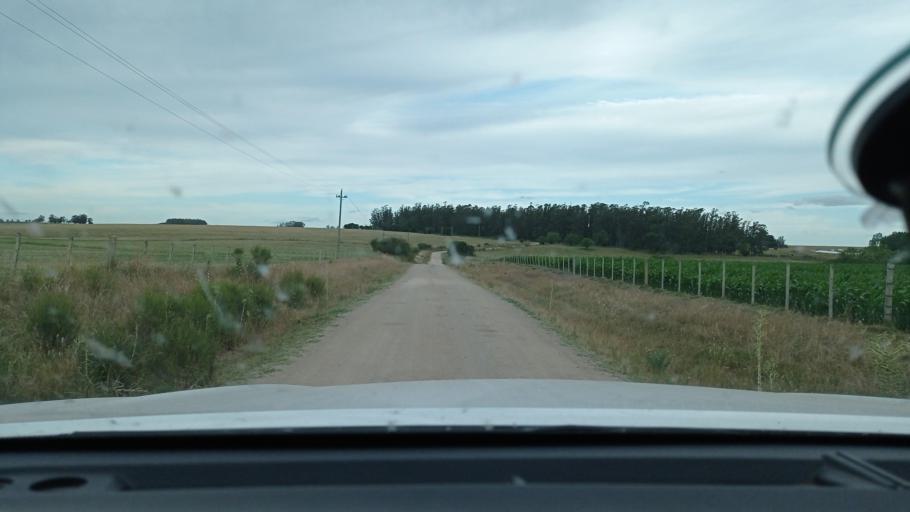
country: UY
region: Florida
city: Casupa
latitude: -34.1010
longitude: -55.7382
